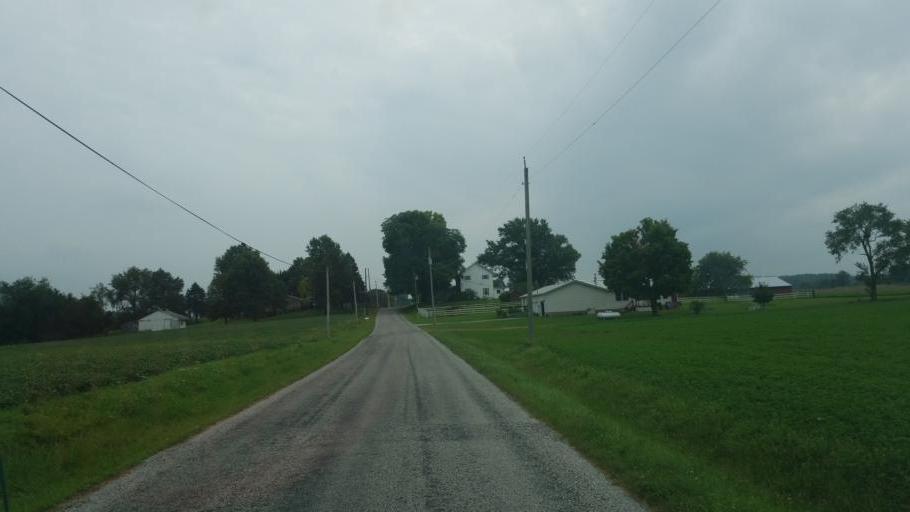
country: US
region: Ohio
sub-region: Wayne County
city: Creston
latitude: 40.9563
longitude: -81.8506
